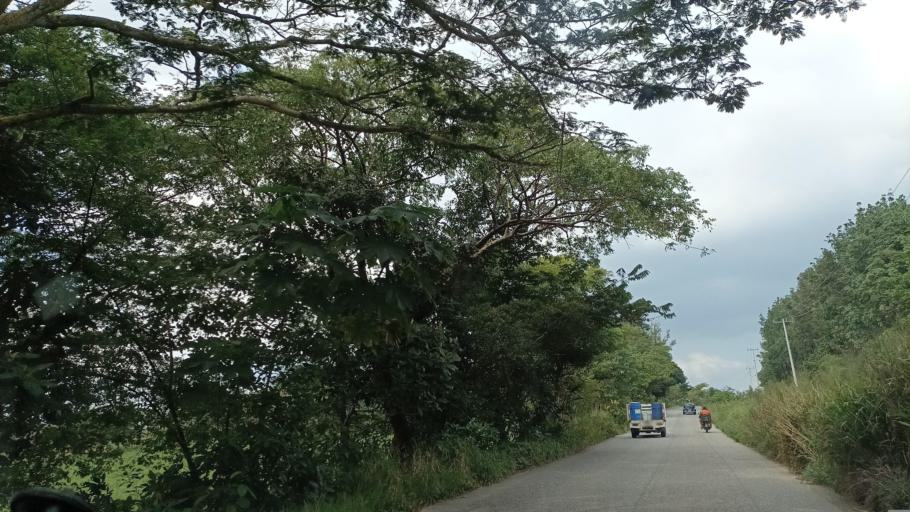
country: MX
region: Veracruz
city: Las Choapas
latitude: 17.8137
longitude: -94.1104
